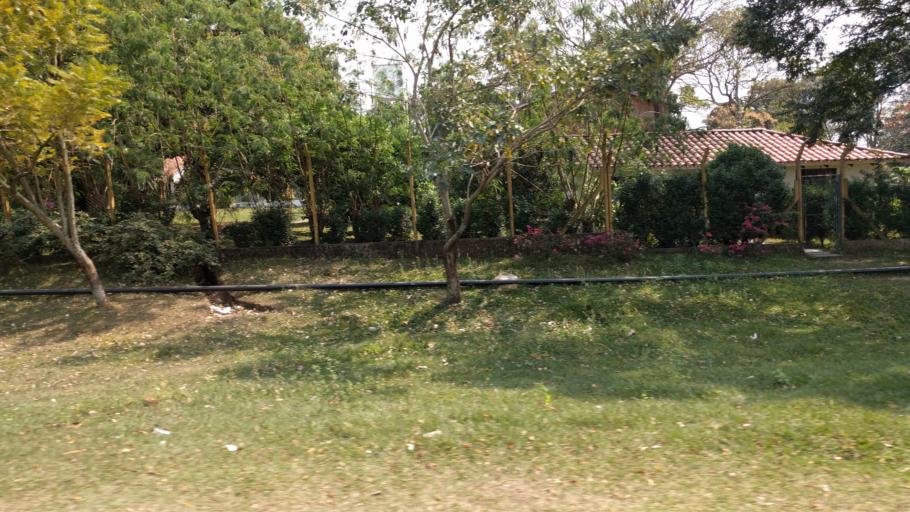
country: BO
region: Santa Cruz
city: Santa Rita
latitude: -17.9332
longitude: -63.3492
